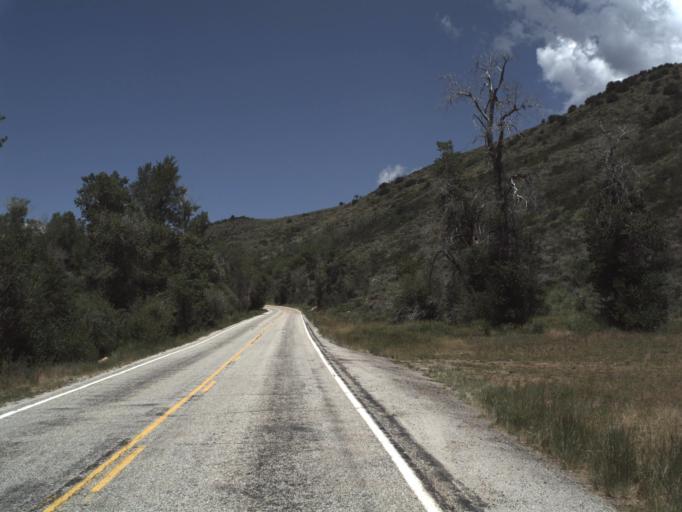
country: US
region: Utah
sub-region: Weber County
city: Wolf Creek
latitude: 41.3697
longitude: -111.5904
